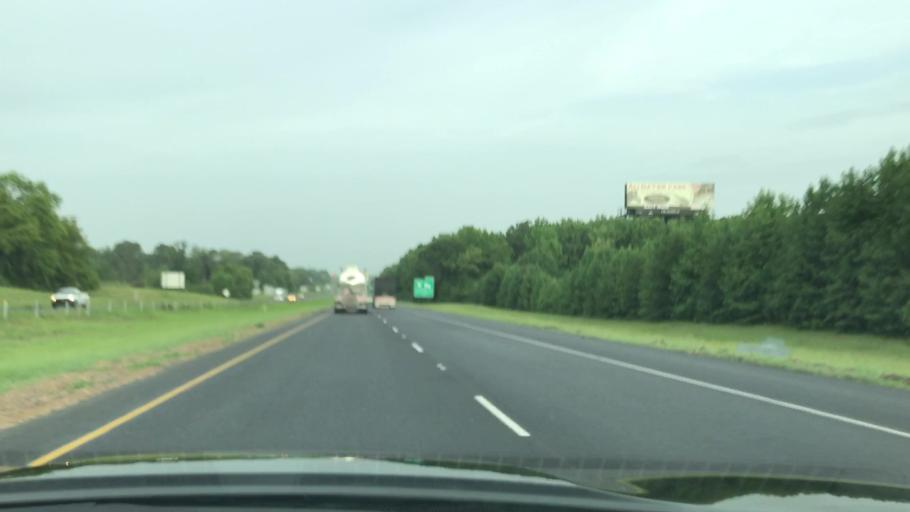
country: US
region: Louisiana
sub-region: Caddo Parish
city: Greenwood
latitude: 32.4451
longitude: -93.9584
